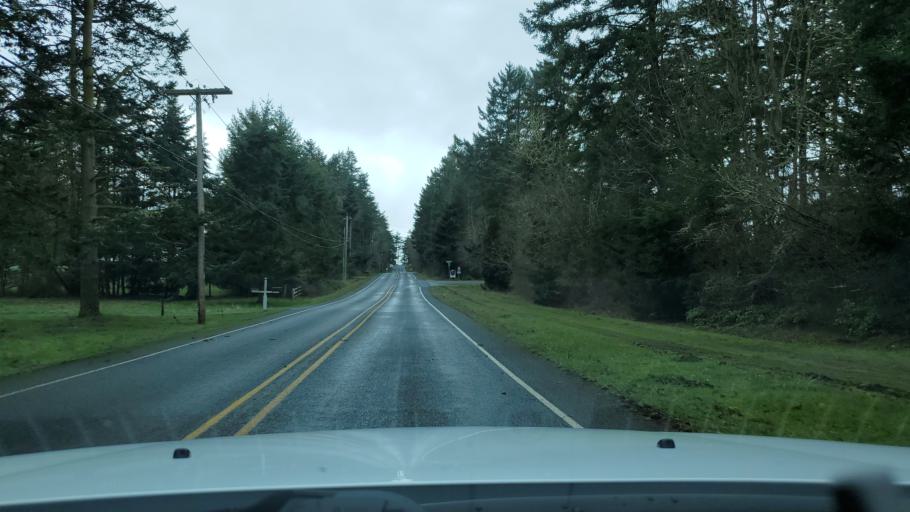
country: US
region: Washington
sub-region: Island County
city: Coupeville
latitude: 48.2319
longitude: -122.7589
